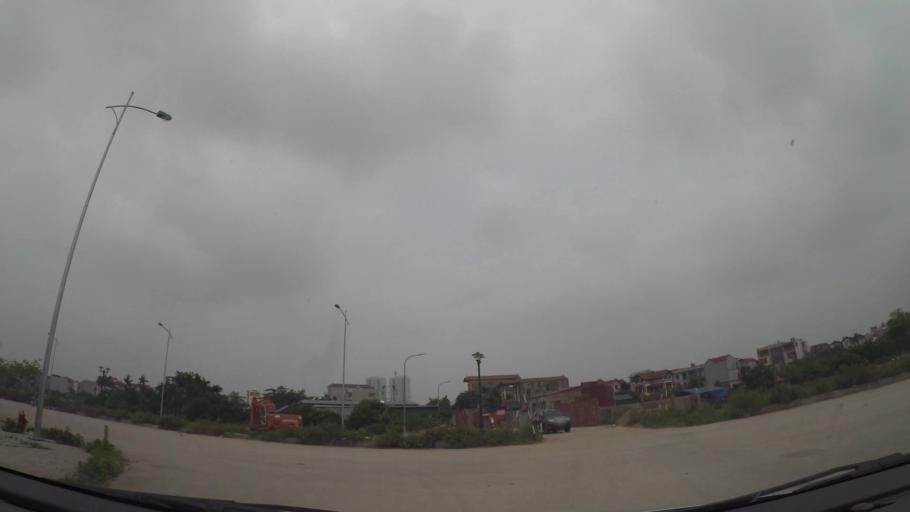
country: VN
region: Ha Noi
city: Ha Dong
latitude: 20.9787
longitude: 105.7517
